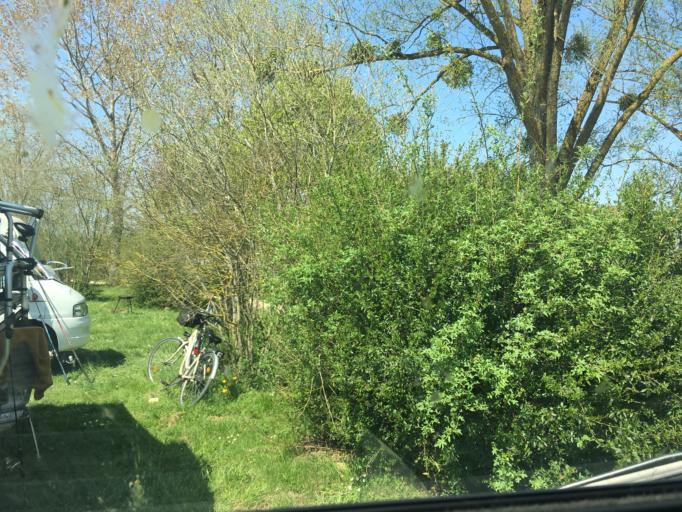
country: FR
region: Lorraine
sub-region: Departement de la Meuse
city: Vigneulles-les-Hattonchatel
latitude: 48.9367
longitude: 5.7155
